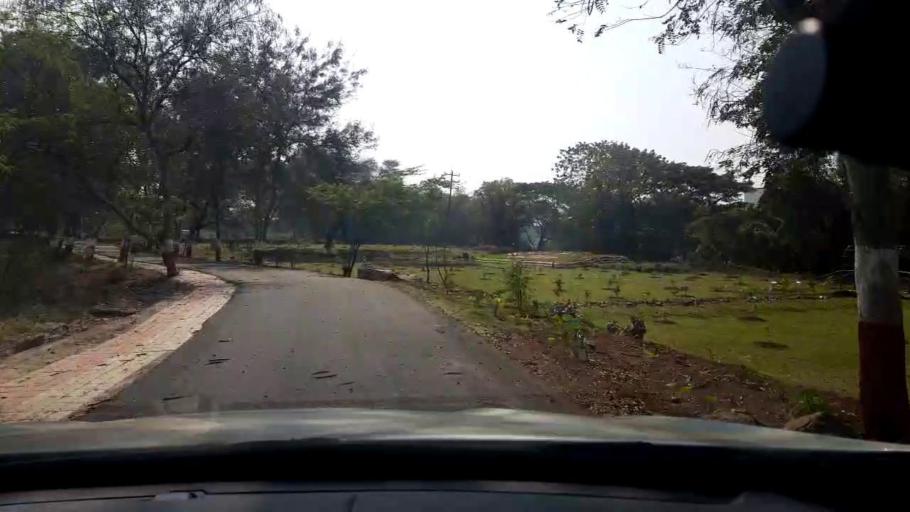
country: IN
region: Maharashtra
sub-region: Pune Division
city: Shivaji Nagar
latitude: 18.5424
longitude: 73.8556
